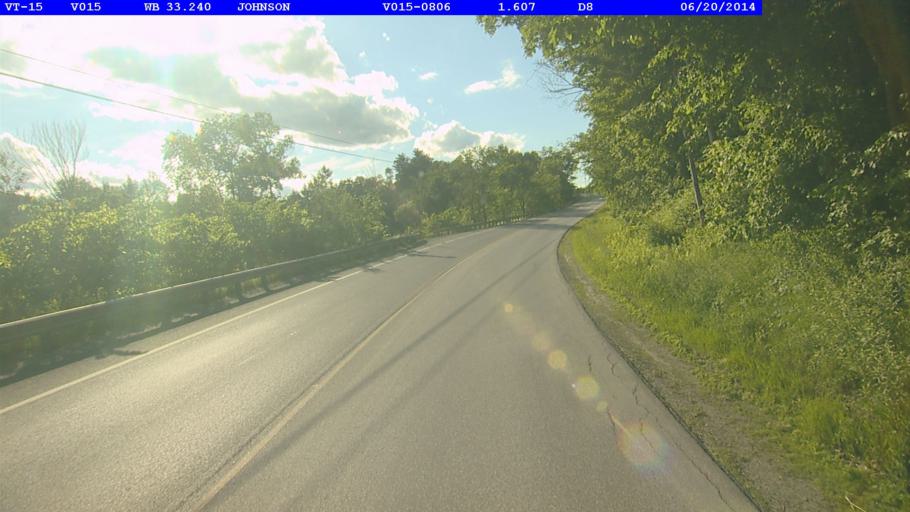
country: US
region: Vermont
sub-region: Lamoille County
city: Johnson
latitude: 44.6426
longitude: -72.7247
